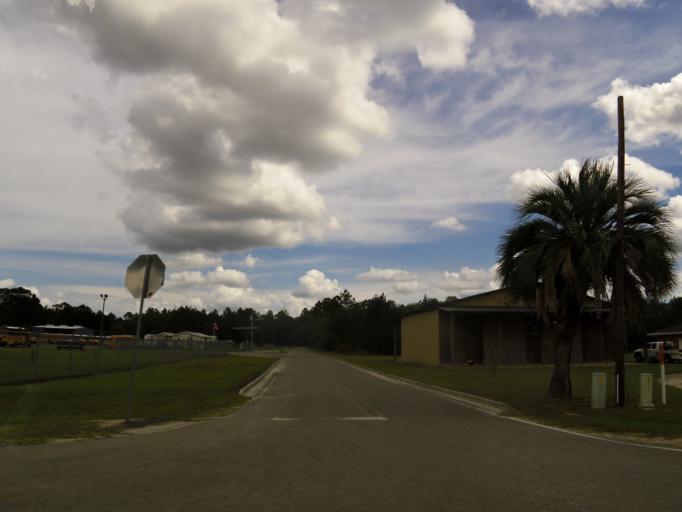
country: US
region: Georgia
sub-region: Brantley County
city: Nahunta
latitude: 31.1968
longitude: -81.9847
